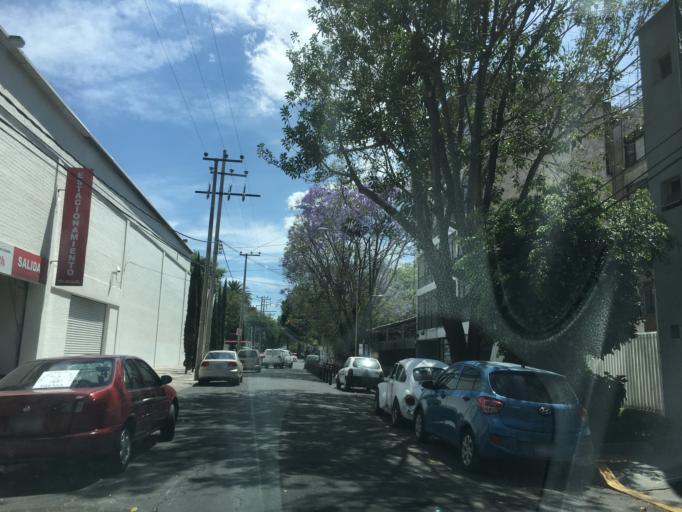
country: MX
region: Mexico City
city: Benito Juarez
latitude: 19.3968
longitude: -99.1568
